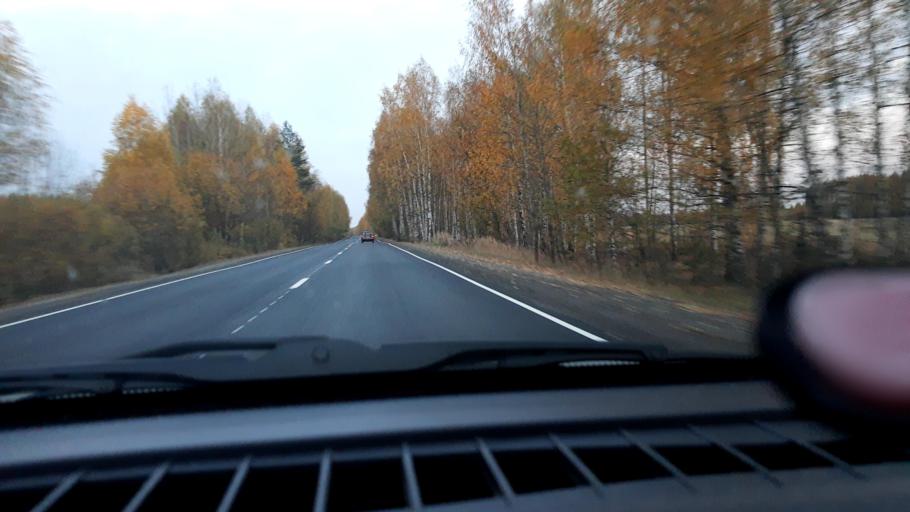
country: RU
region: Nizjnij Novgorod
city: Novaya Balakhna
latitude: 56.5601
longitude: 43.7310
